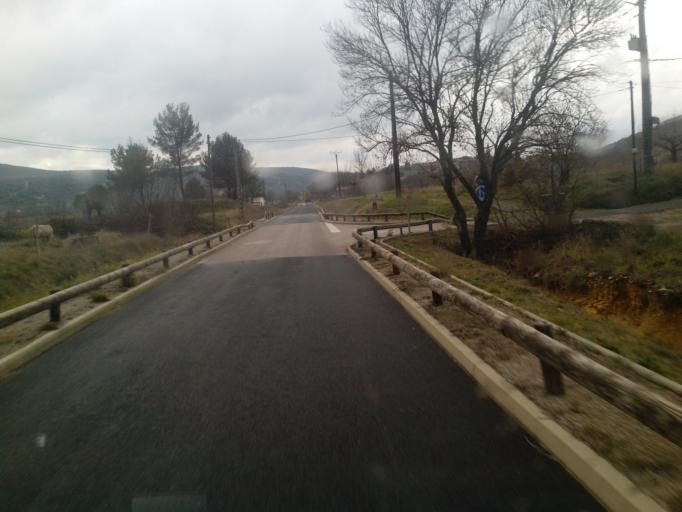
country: FR
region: Languedoc-Roussillon
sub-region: Departement du Gard
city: Saint-Hippolyte-du-Fort
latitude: 43.9316
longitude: 3.7968
